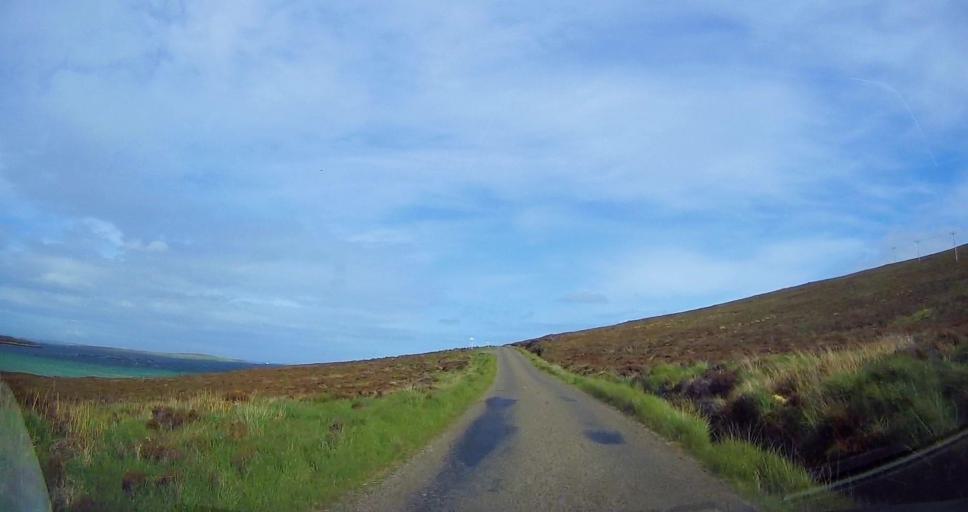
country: GB
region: Scotland
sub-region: Orkney Islands
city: Stromness
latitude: 58.8688
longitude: -3.2310
